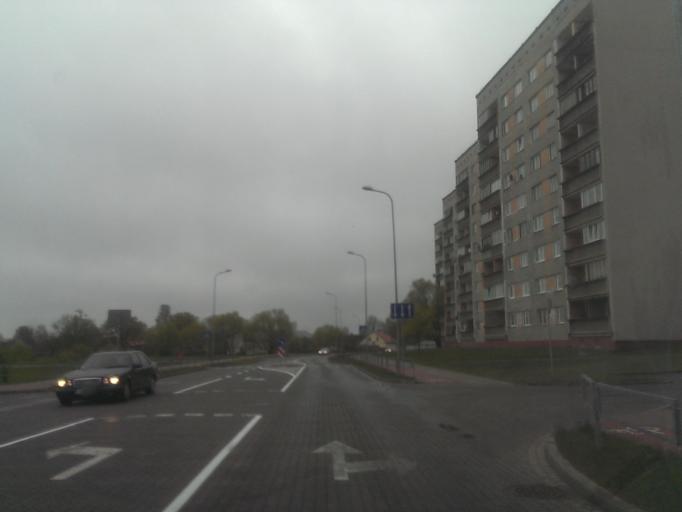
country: LV
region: Ventspils
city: Ventspils
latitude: 57.4057
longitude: 21.6023
